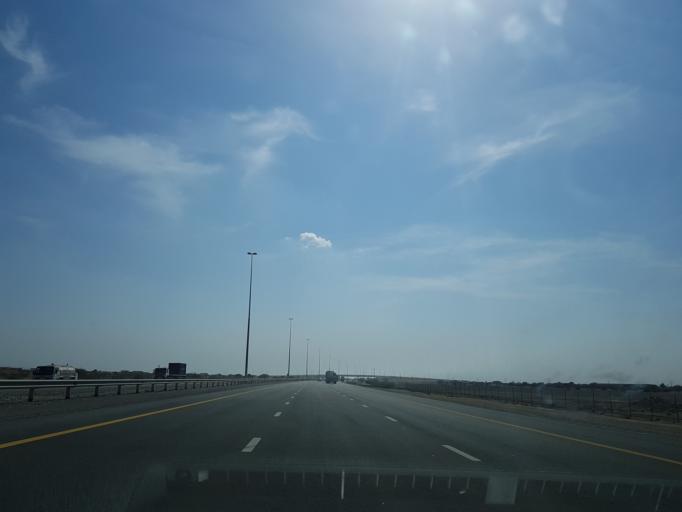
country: AE
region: Ra's al Khaymah
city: Ras al-Khaimah
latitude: 25.7250
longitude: 56.0118
